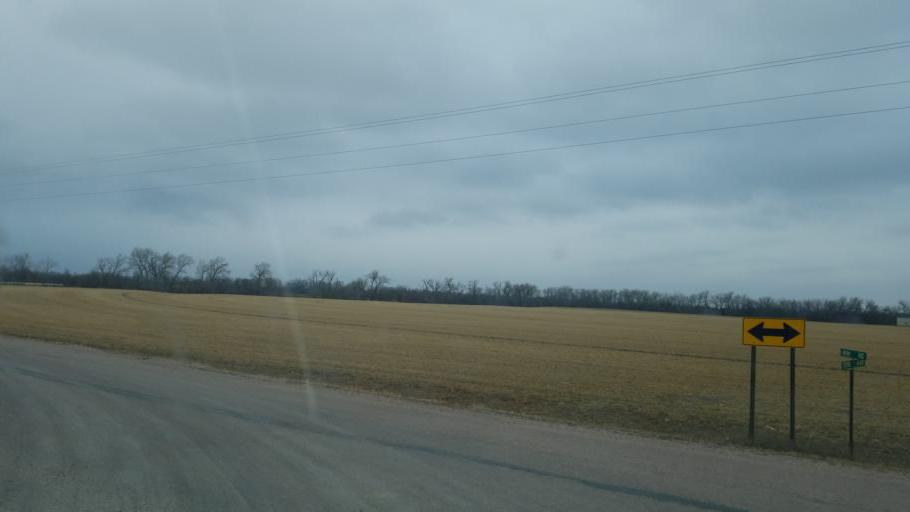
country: US
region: South Dakota
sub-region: Yankton County
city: Yankton
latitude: 42.8446
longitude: -97.3822
